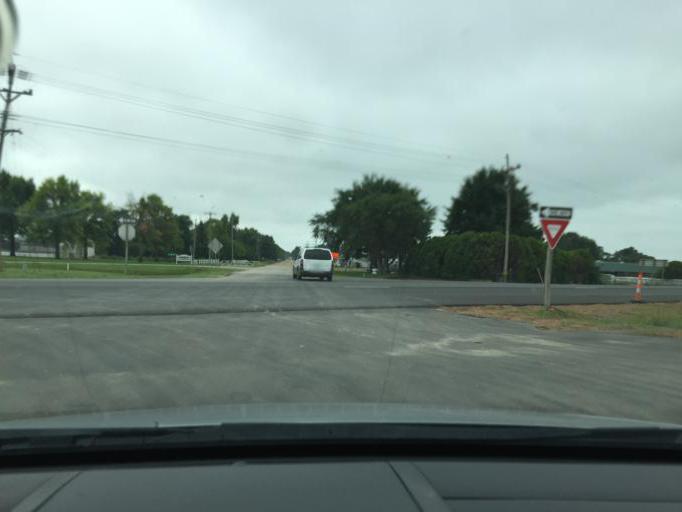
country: US
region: Kansas
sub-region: Reno County
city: South Hutchinson
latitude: 37.9975
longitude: -98.0320
